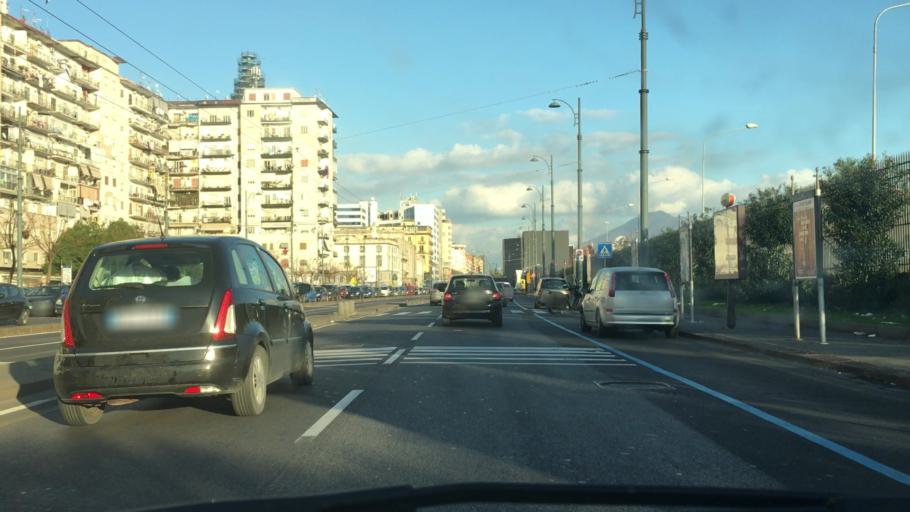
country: IT
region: Campania
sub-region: Provincia di Napoli
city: Napoli
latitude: 40.8459
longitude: 14.2646
